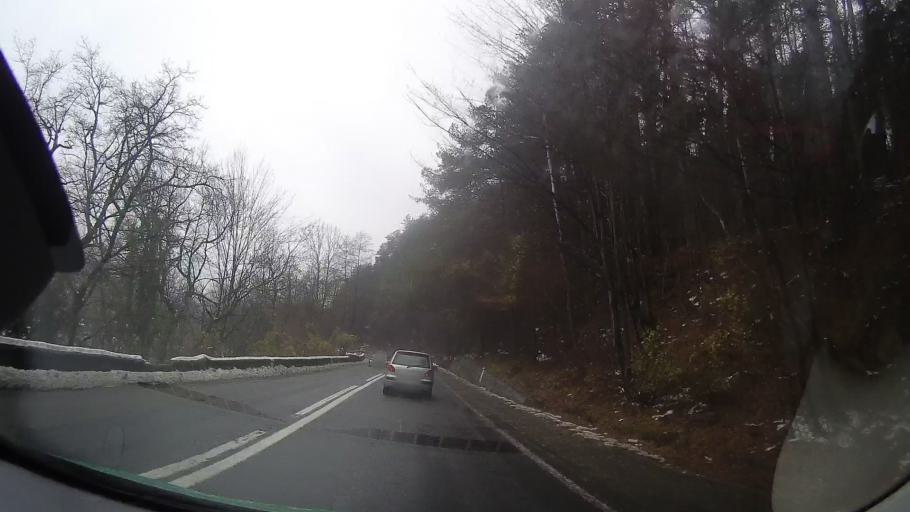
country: RO
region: Neamt
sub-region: Comuna Tarcau
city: Tarcau
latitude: 46.8970
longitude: 26.1219
